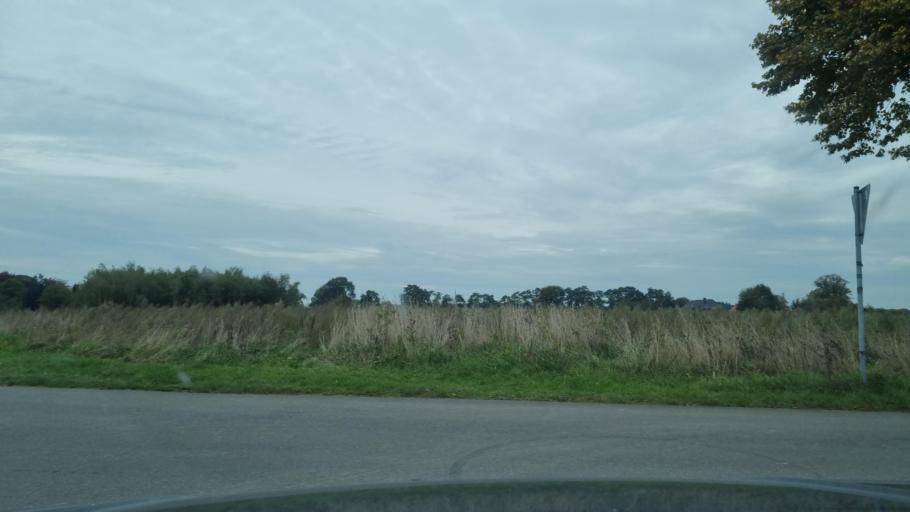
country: DE
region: North Rhine-Westphalia
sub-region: Regierungsbezirk Dusseldorf
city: Kleve
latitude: 51.7450
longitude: 6.2021
